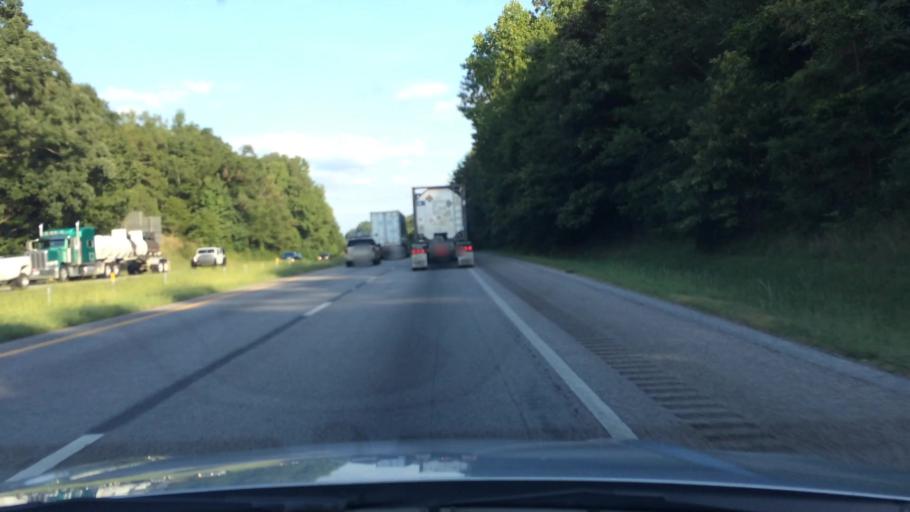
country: US
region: South Carolina
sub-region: Laurens County
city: Clinton
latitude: 34.4894
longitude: -81.8360
